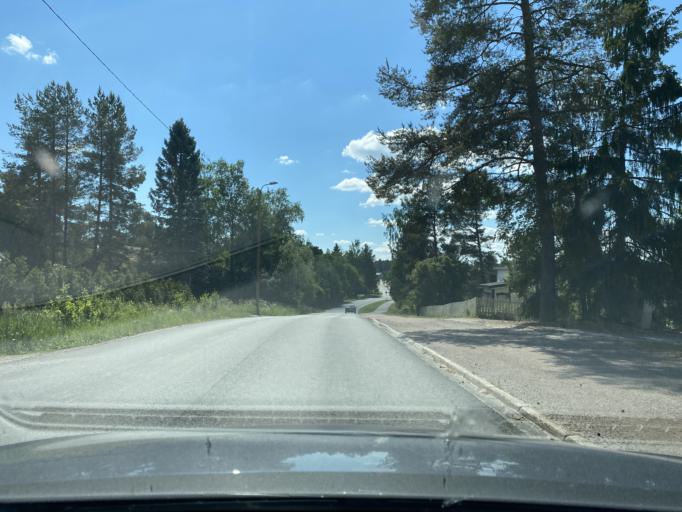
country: FI
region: Satakunta
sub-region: Rauma
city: Eura
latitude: 61.1260
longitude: 22.1623
